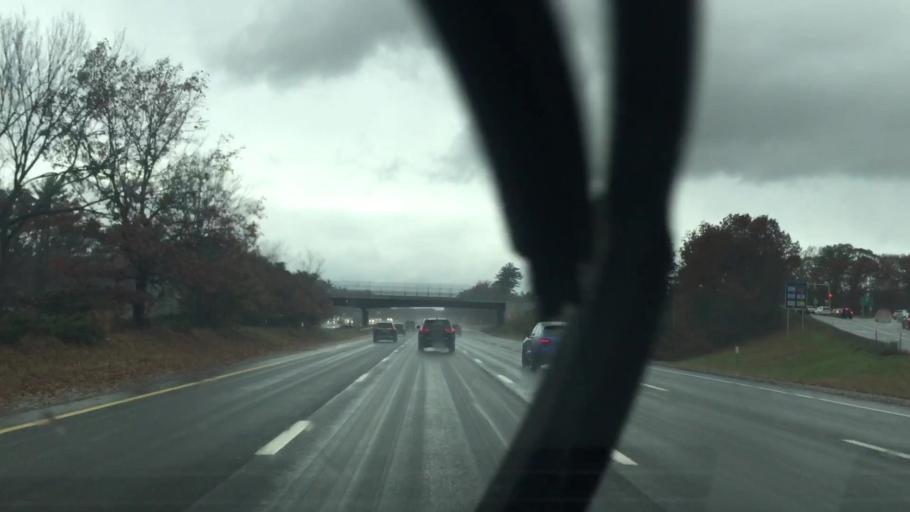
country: US
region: New Hampshire
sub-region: Rockingham County
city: Seabrook
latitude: 42.8929
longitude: -70.8801
